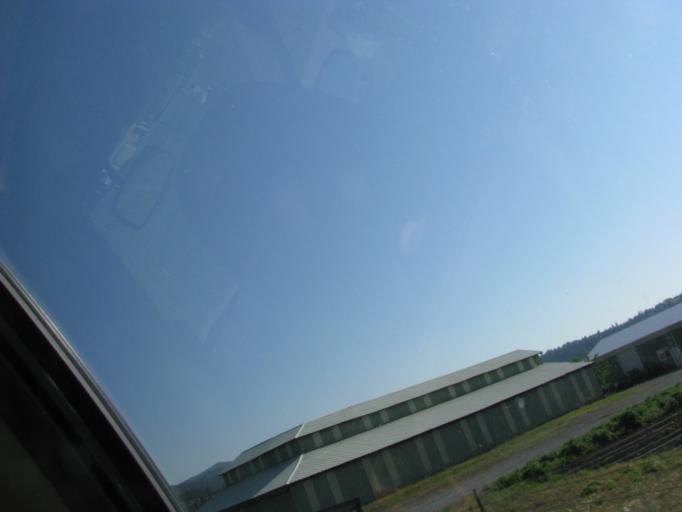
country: US
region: Washington
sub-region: Spokane County
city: Liberty Lake
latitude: 47.6270
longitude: -117.1138
